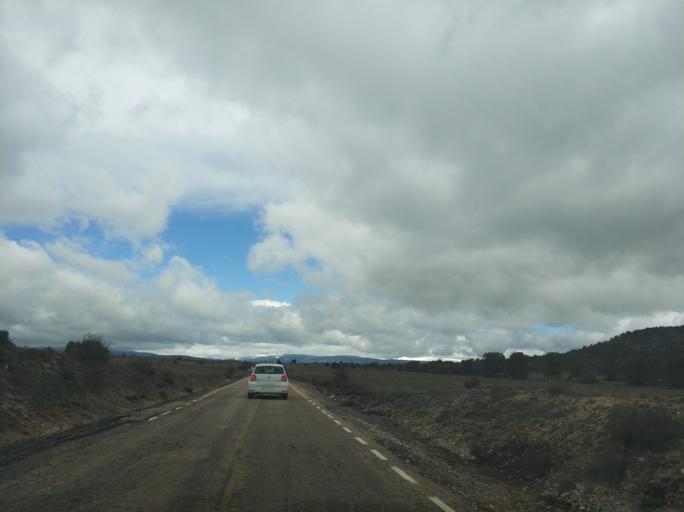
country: ES
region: Castille and Leon
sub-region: Provincia de Soria
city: Abejar
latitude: 41.7923
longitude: -2.7685
